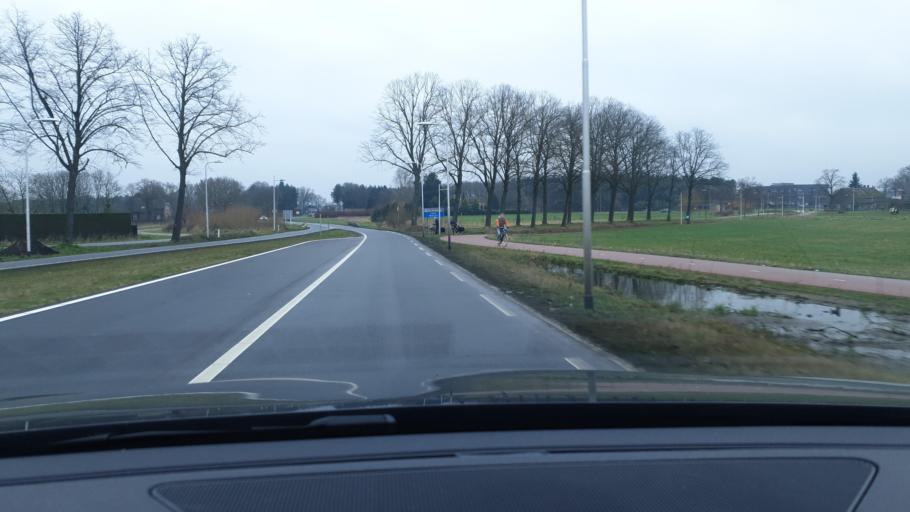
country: NL
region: North Brabant
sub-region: Gemeente Veldhoven
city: Oerle
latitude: 51.3993
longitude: 5.3779
